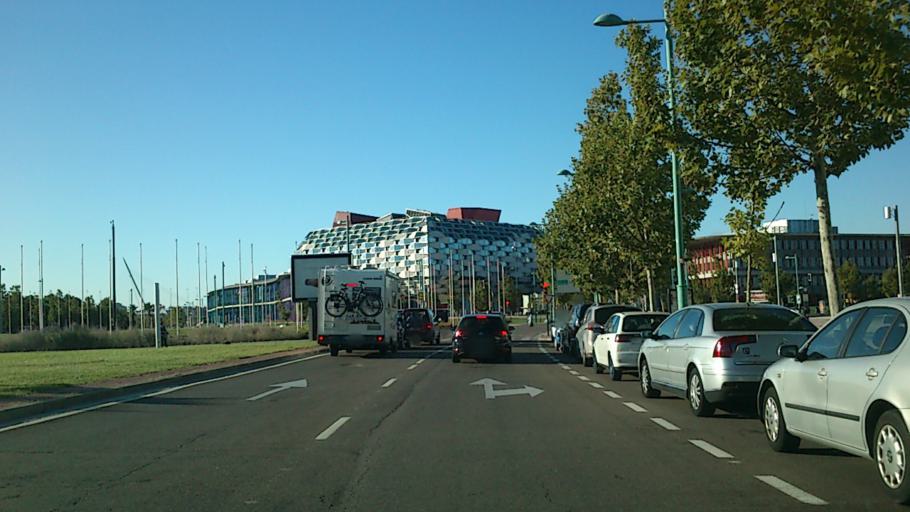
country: ES
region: Aragon
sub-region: Provincia de Zaragoza
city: Almozara
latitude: 41.6729
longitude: -0.8979
